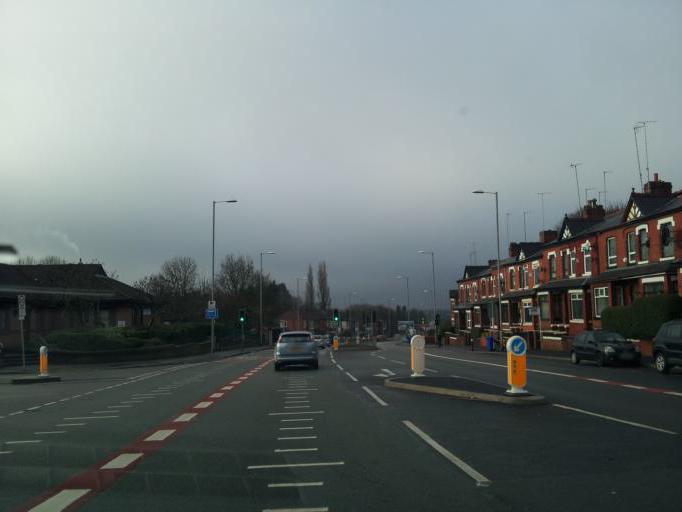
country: GB
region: England
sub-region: Manchester
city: Blackley
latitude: 53.5267
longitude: -2.2125
